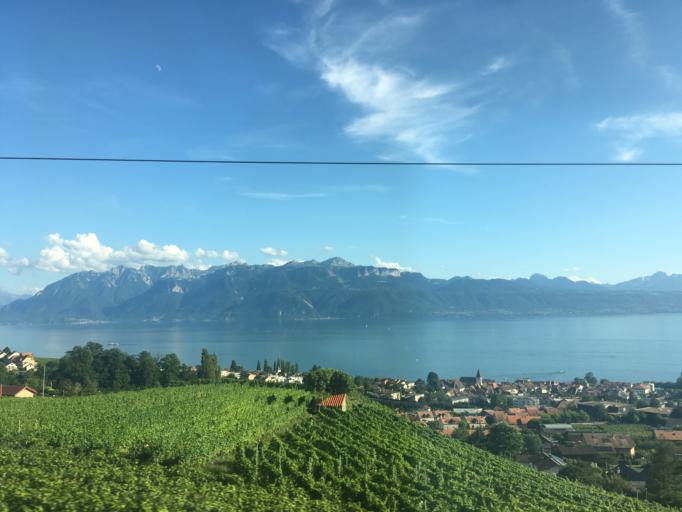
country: CH
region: Vaud
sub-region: Lavaux-Oron District
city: Lutry
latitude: 46.5114
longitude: 6.6868
